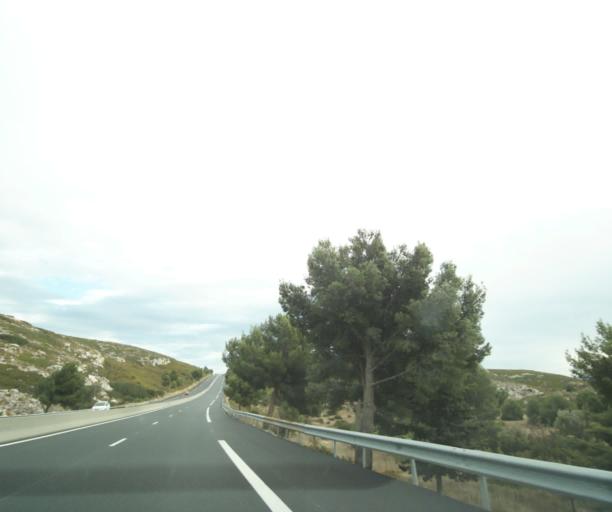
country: FR
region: Provence-Alpes-Cote d'Azur
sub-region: Departement des Bouches-du-Rhone
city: Sausset-les-Pins
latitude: 43.3432
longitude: 5.1277
